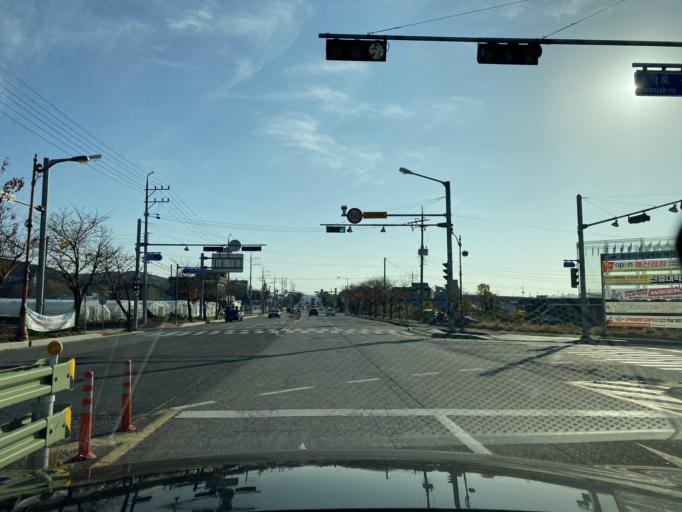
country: KR
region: Chungcheongnam-do
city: Yesan
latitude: 36.7082
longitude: 126.8399
